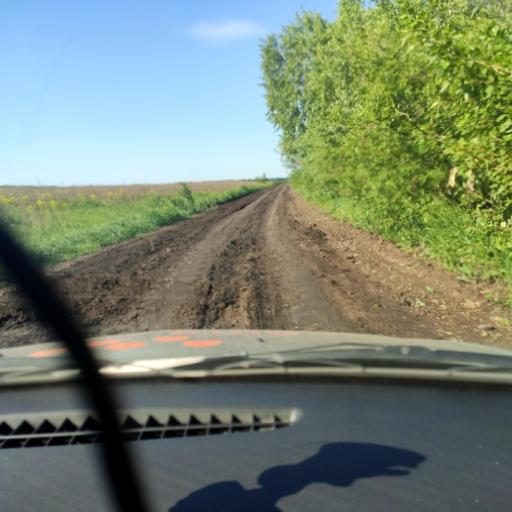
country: RU
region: Bashkortostan
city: Avdon
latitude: 54.5721
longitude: 55.8395
